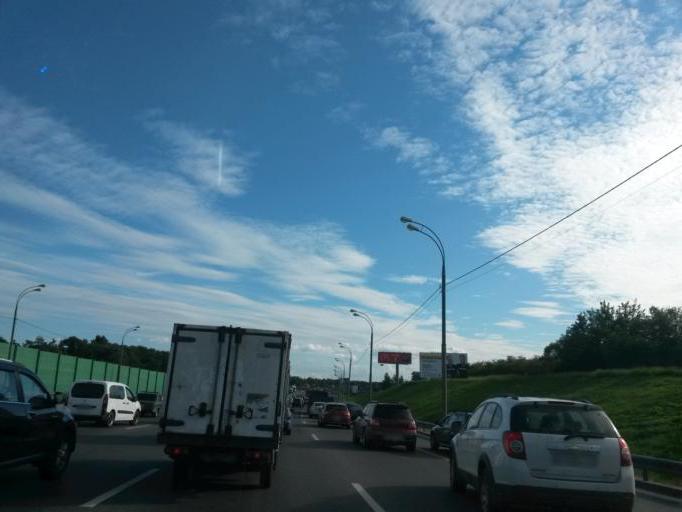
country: RU
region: Moskovskaya
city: Vidnoye
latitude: 55.5586
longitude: 37.6869
